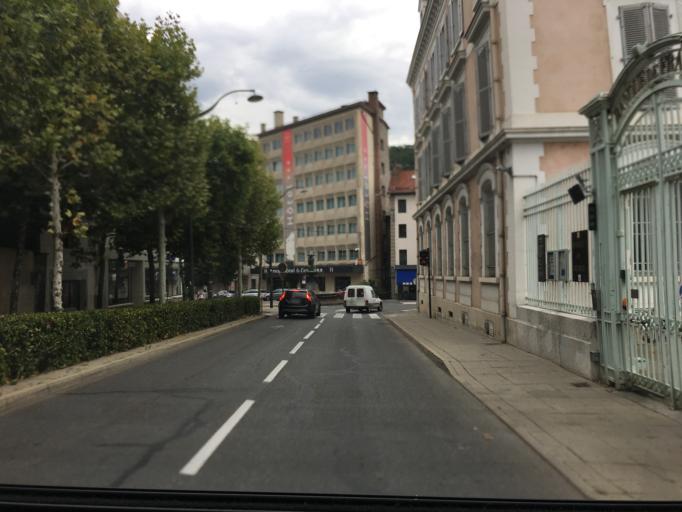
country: FR
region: Provence-Alpes-Cote d'Azur
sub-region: Departement des Hautes-Alpes
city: Gap
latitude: 44.5568
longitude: 6.0761
